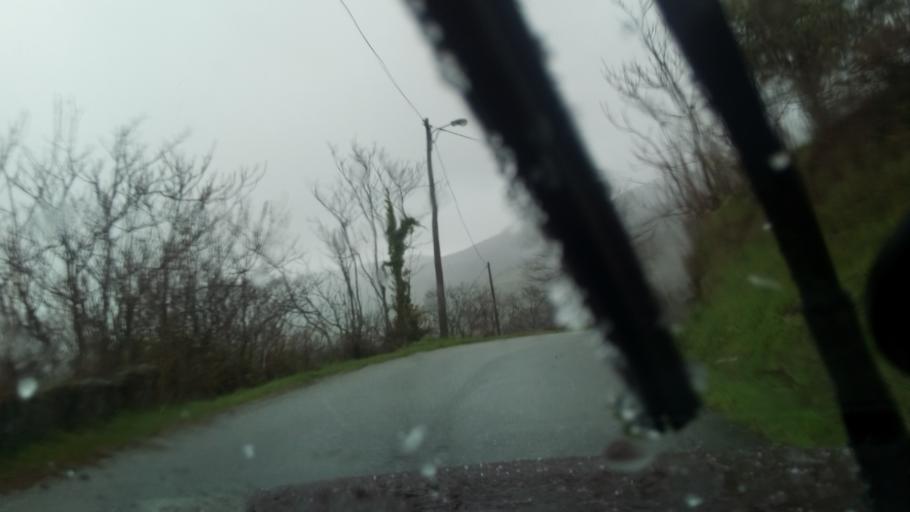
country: PT
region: Guarda
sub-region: Fornos de Algodres
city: Fornos de Algodres
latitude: 40.5428
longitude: -7.4612
